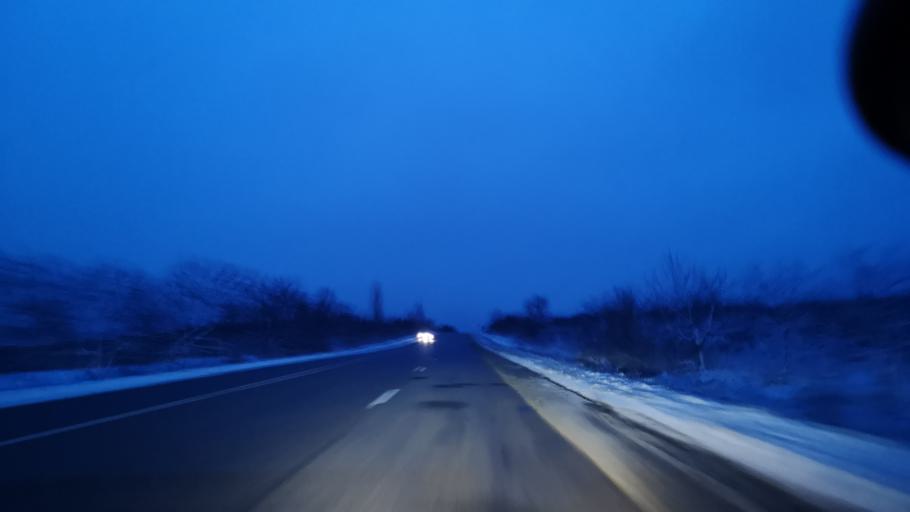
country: MD
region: Orhei
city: Orhei
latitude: 47.5396
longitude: 28.7931
